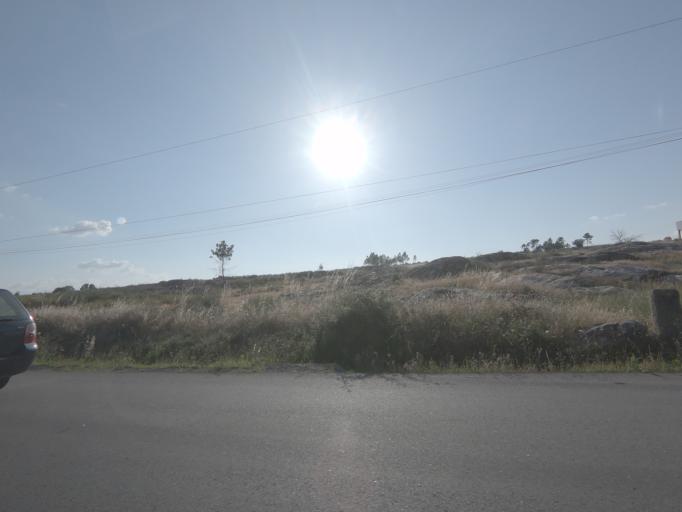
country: PT
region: Vila Real
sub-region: Chaves
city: Chaves
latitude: 41.7863
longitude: -7.4352
